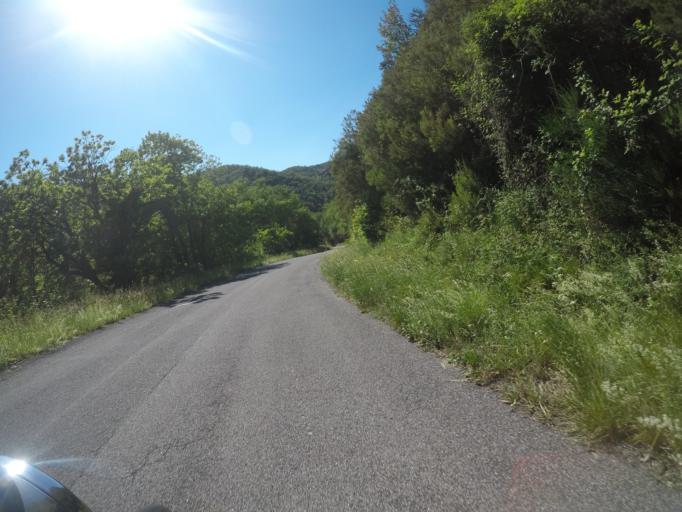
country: IT
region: Tuscany
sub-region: Provincia di Massa-Carrara
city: Fosdinovo
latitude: 44.1435
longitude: 10.0875
